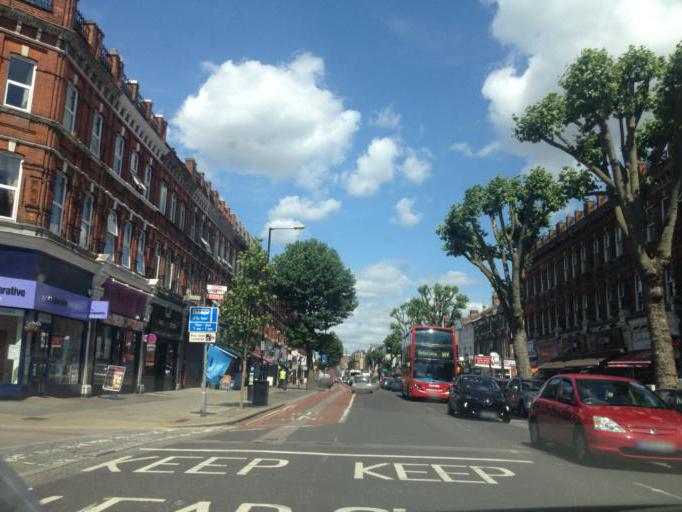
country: GB
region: England
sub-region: Greater London
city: Belsize Park
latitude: 51.5544
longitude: -0.2126
